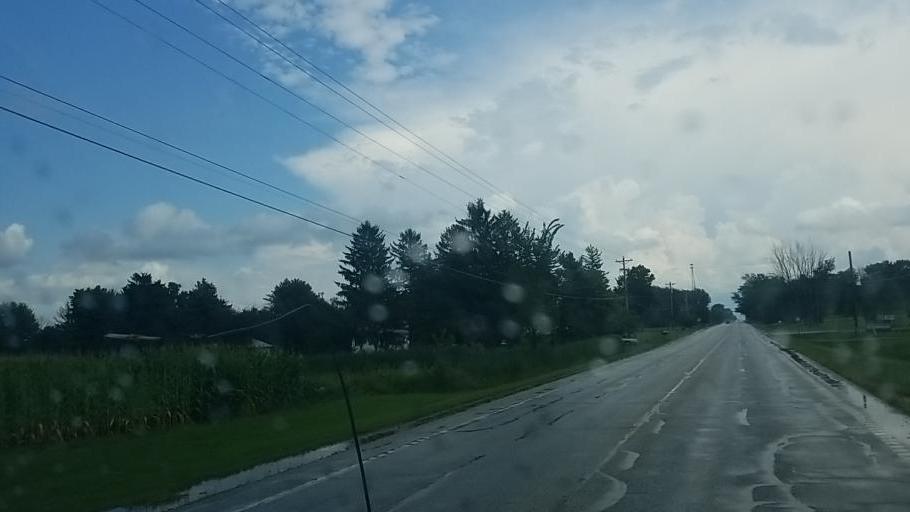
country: US
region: Ohio
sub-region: Lorain County
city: Grafton
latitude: 41.1679
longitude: -82.0170
